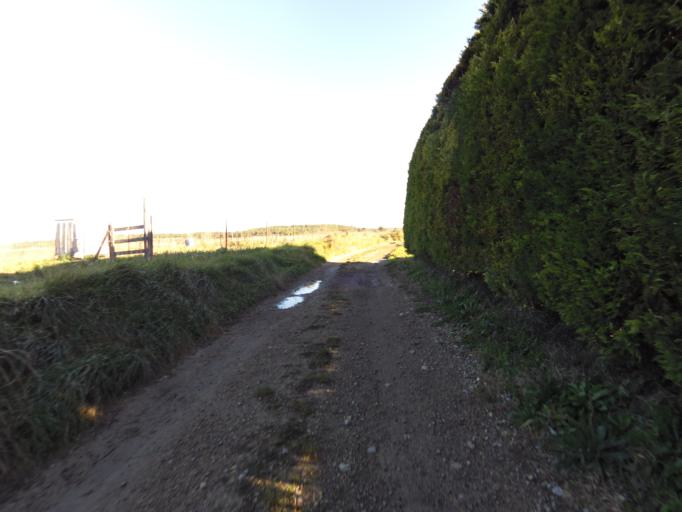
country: FR
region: Languedoc-Roussillon
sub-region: Departement du Gard
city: Aigues-Vives
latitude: 43.7446
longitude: 4.1861
